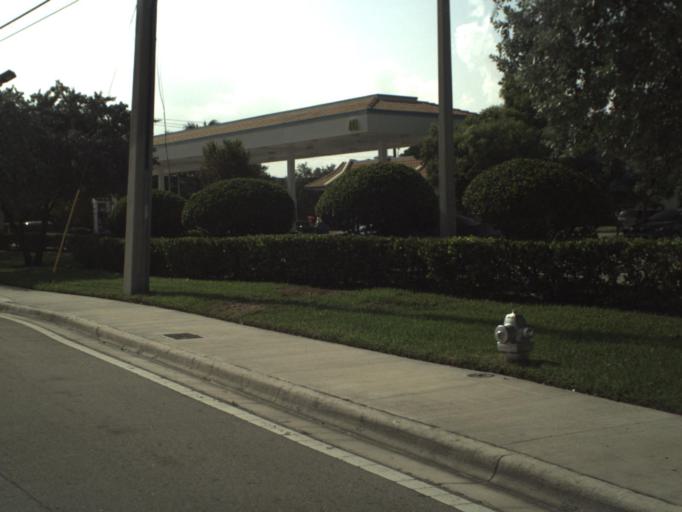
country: US
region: Florida
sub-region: Broward County
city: Coral Springs
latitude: 26.2729
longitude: -80.2814
